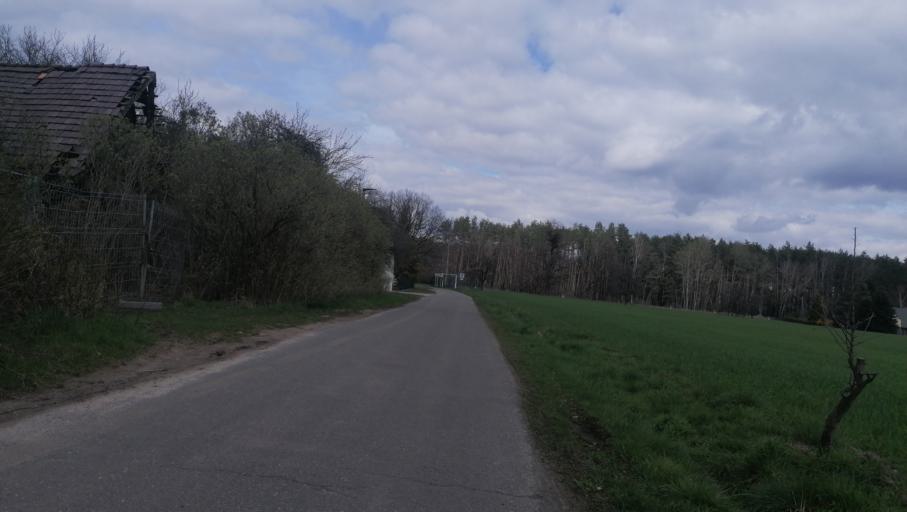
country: DE
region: Brandenburg
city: Cottbus
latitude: 51.6841
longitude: 14.3395
